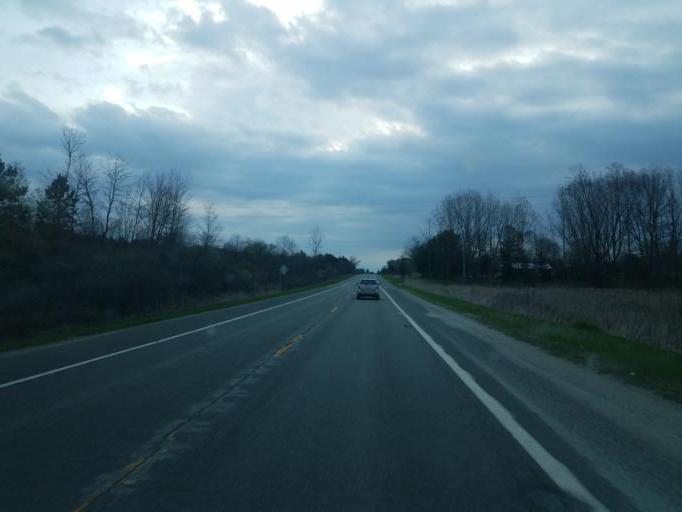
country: US
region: Michigan
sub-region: Isabella County
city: Lake Isabella
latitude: 43.5970
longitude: -84.9419
